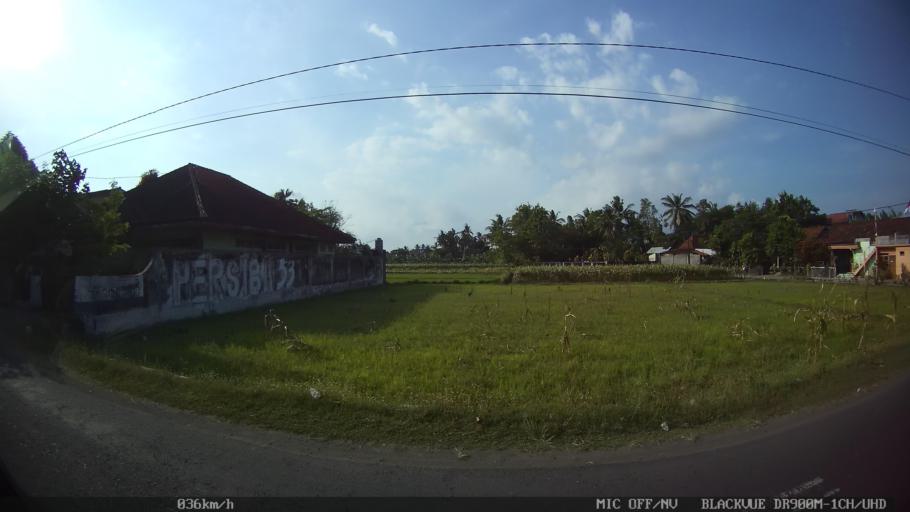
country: ID
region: Daerah Istimewa Yogyakarta
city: Bantul
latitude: -7.8905
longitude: 110.3215
